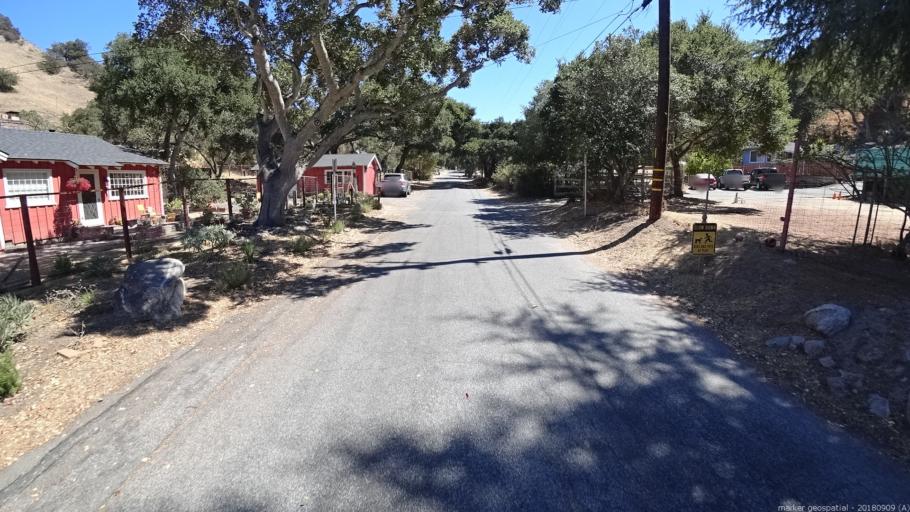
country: US
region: California
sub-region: Monterey County
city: Carmel Valley Village
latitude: 36.5653
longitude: -121.6970
